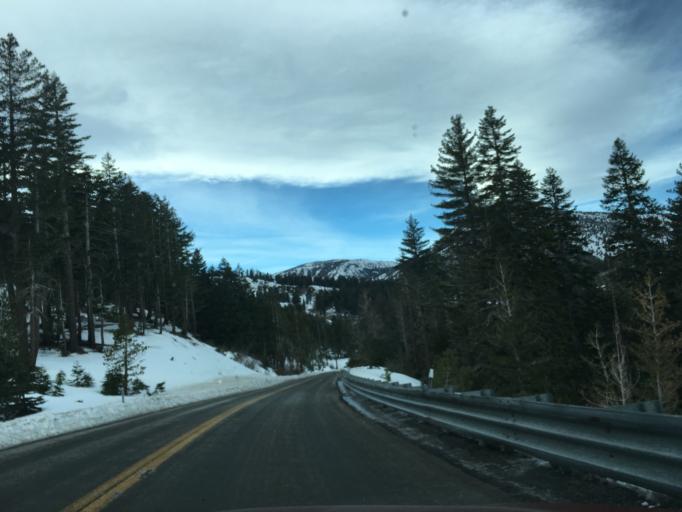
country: US
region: Nevada
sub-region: Washoe County
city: Incline Village
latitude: 39.3241
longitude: -119.8708
